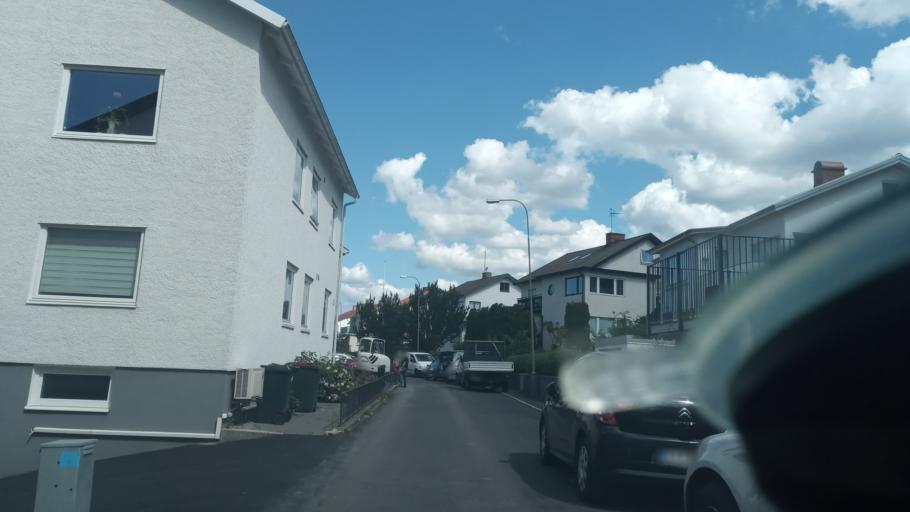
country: SE
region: Vaestra Goetaland
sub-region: Molndal
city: Moelndal
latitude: 57.6924
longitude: 12.0057
